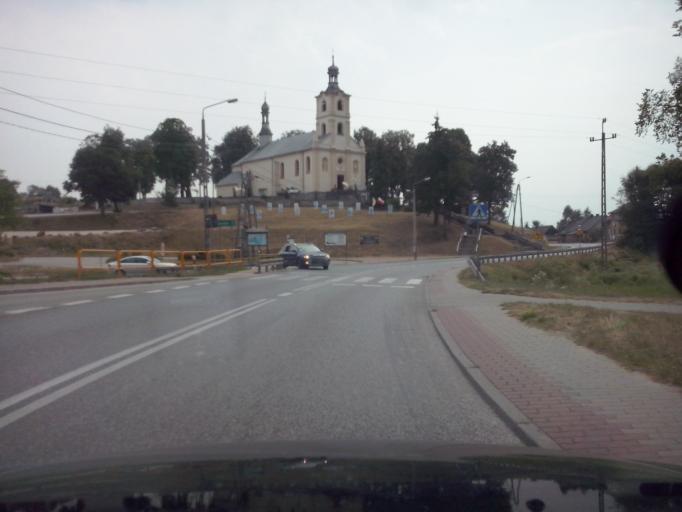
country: PL
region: Swietokrzyskie
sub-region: Powiat kielecki
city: Brzeziny
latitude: 50.7729
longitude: 20.5733
